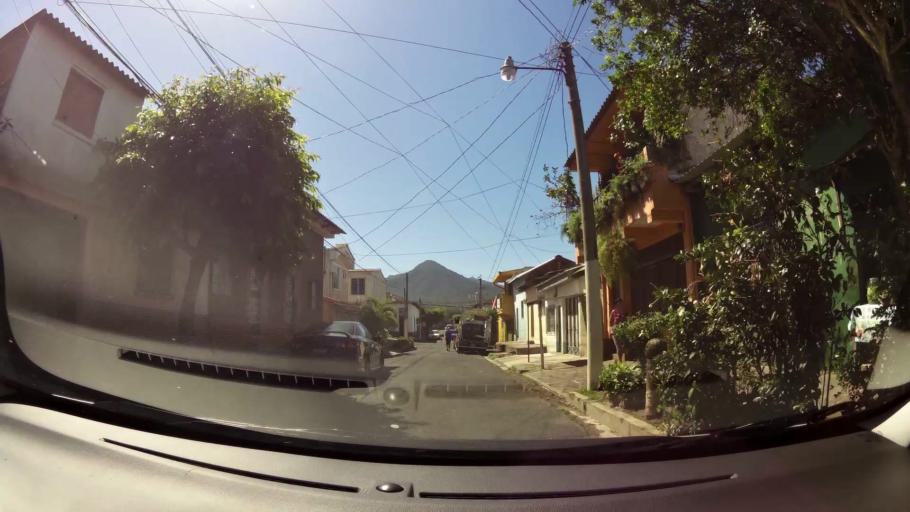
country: SV
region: Ahuachapan
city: Ahuachapan
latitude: 13.9197
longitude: -89.8446
